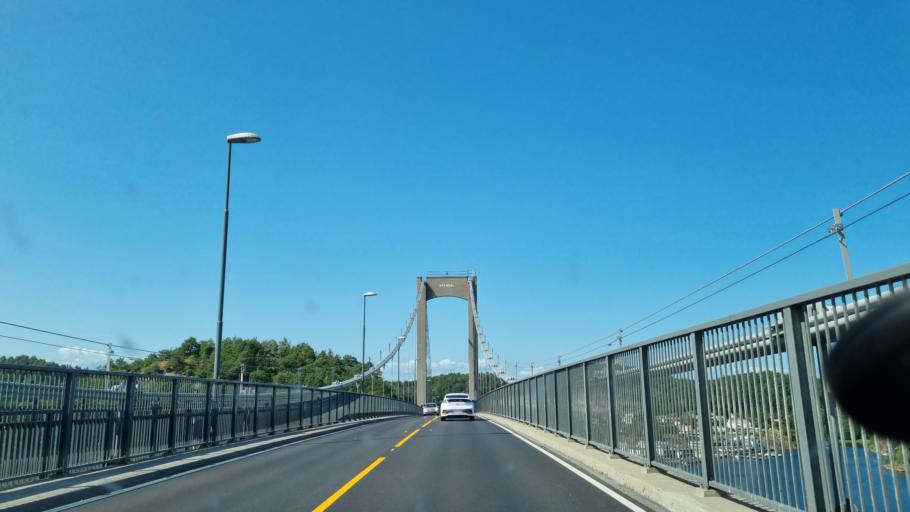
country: NO
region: Aust-Agder
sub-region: Arendal
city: Arendal
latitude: 58.4709
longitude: 8.8229
